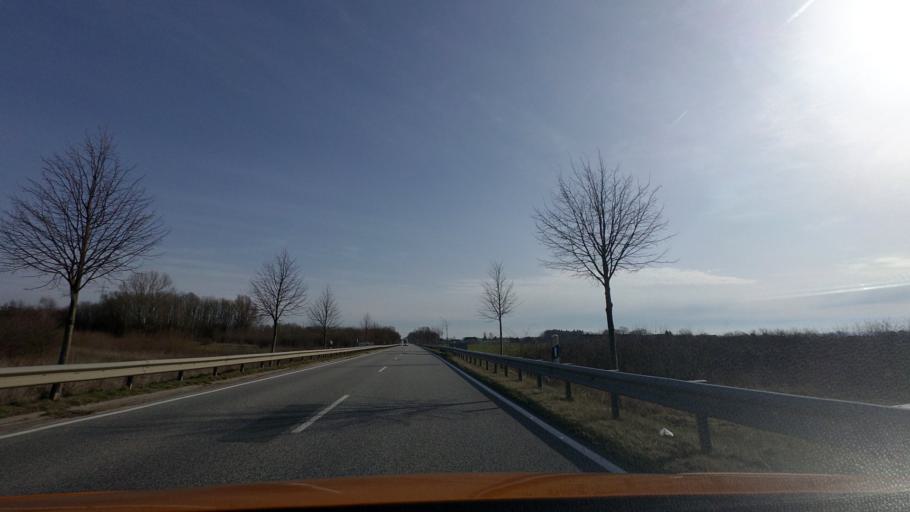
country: DE
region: North Rhine-Westphalia
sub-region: Regierungsbezirk Detmold
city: Petershagen
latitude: 52.3737
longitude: 9.0310
